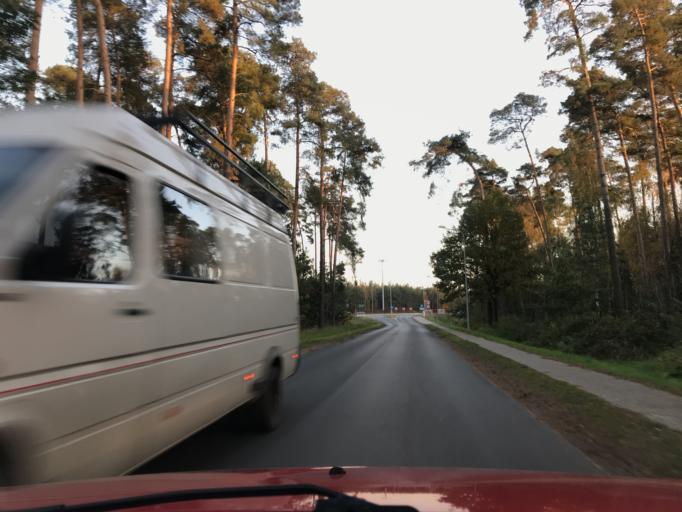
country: PL
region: Greater Poland Voivodeship
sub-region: Powiat poznanski
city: Baranowo
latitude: 52.3890
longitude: 16.7437
